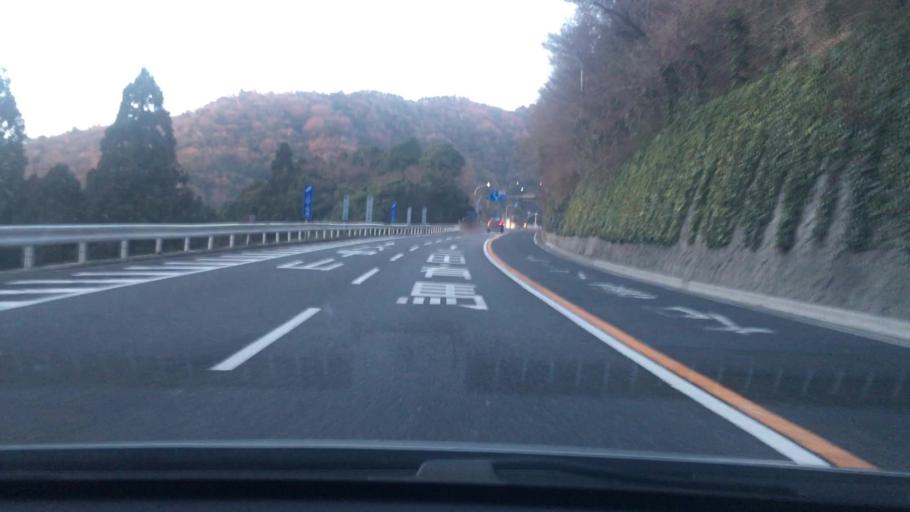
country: JP
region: Hyogo
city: Kobe
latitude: 34.7453
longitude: 135.2290
